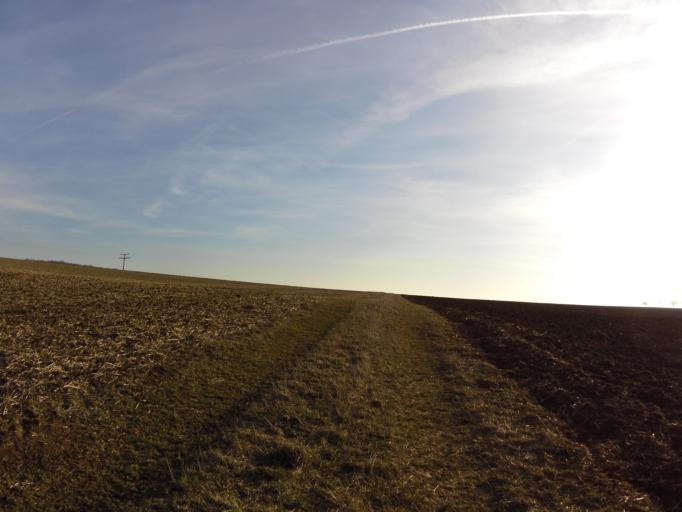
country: DE
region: Bavaria
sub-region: Regierungsbezirk Unterfranken
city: Kurnach
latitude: 49.8339
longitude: 10.0337
